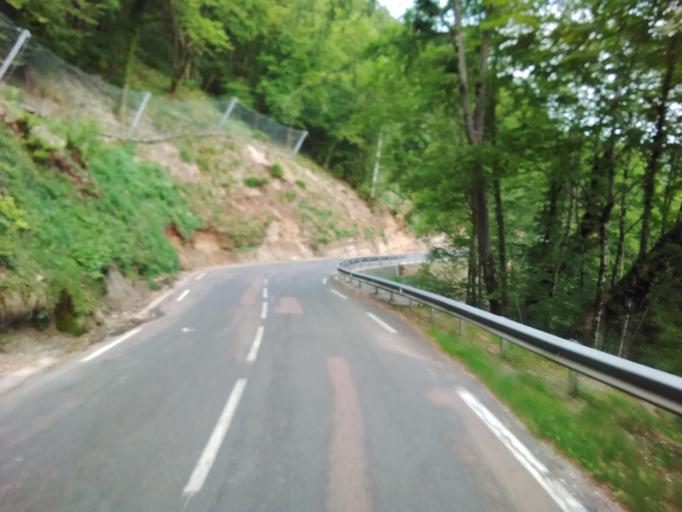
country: FR
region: Franche-Comte
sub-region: Departement du Jura
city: Arbois
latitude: 46.8700
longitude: 5.8032
